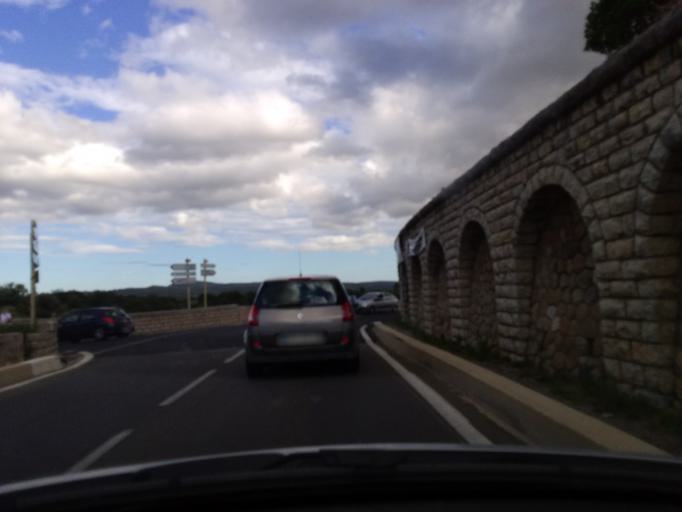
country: FR
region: Languedoc-Roussillon
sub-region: Departement de l'Herault
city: Saint-Jean-de-Fos
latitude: 43.7080
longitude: 3.5566
